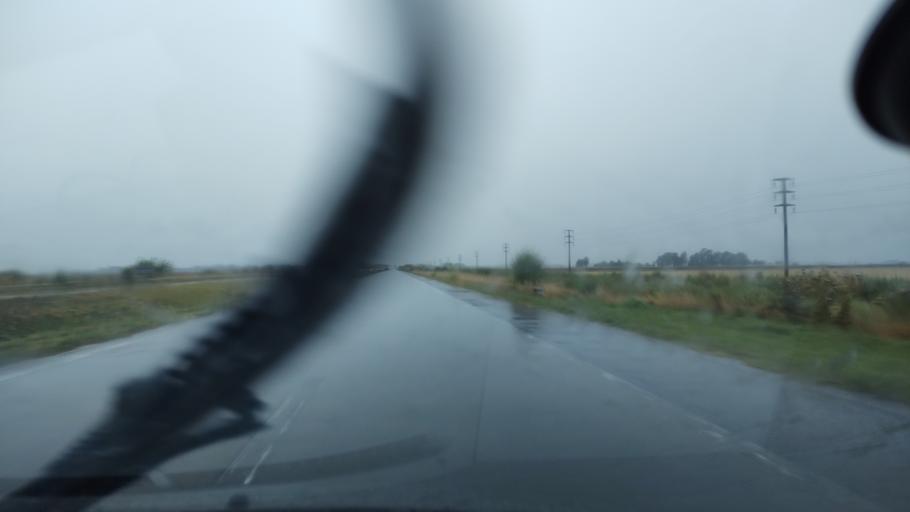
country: AR
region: Buenos Aires
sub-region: Partido de San Vicente
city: San Vicente
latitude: -35.0645
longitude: -58.4764
